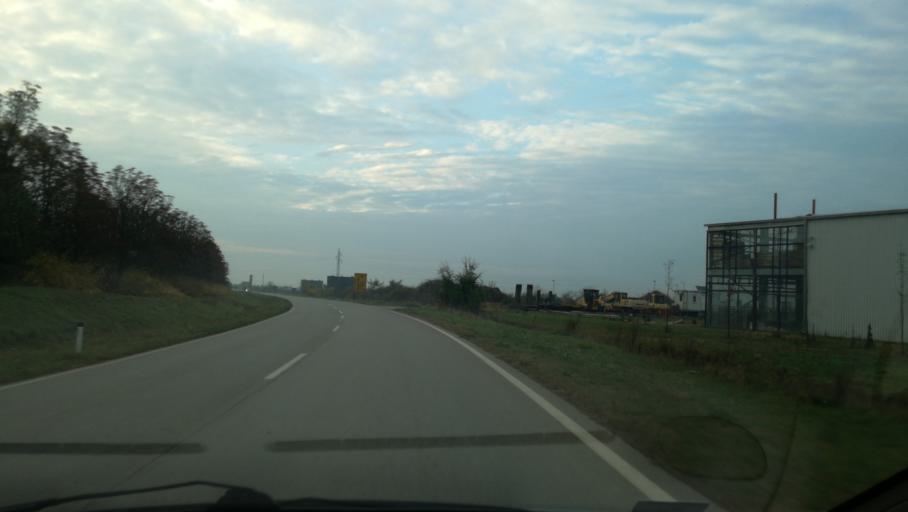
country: RS
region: Autonomna Pokrajina Vojvodina
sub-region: Severnobanatski Okrug
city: Kikinda
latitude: 45.8090
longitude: 20.4326
